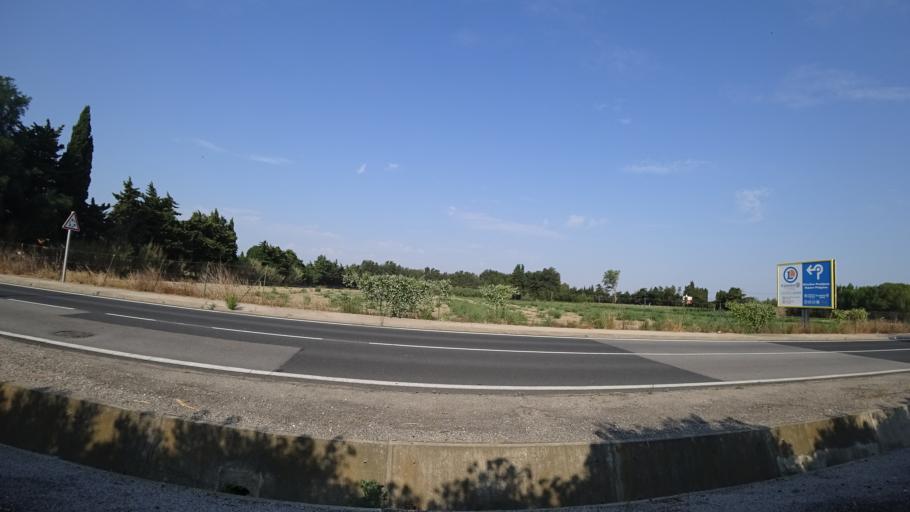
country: FR
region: Languedoc-Roussillon
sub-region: Departement des Pyrenees-Orientales
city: Bompas
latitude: 42.7176
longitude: 2.9323
